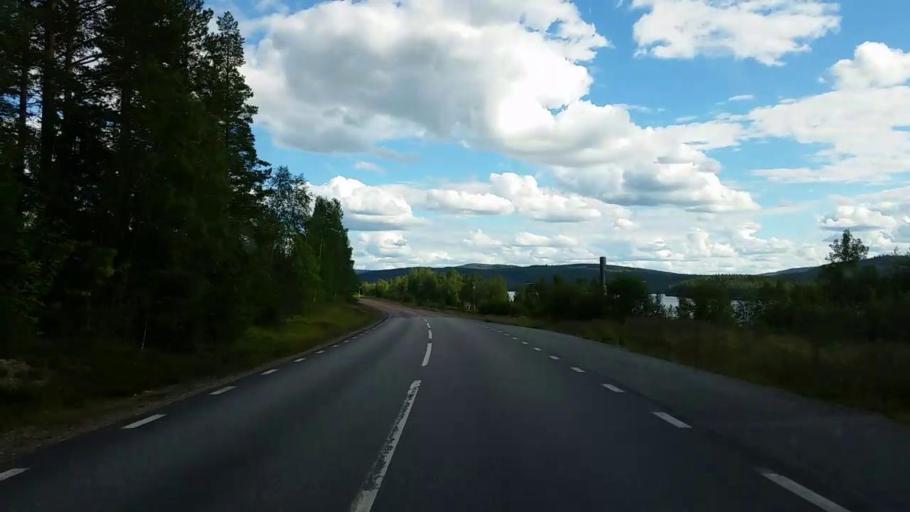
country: SE
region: Gaevleborg
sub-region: Ljusdals Kommun
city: Farila
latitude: 62.1391
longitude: 15.6889
